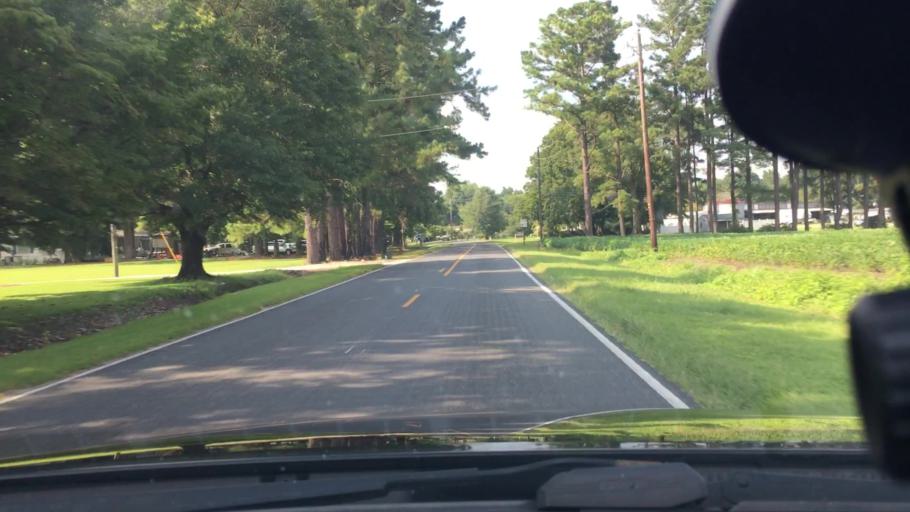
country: US
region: North Carolina
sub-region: Craven County
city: New Bern
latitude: 35.1719
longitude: -77.0511
